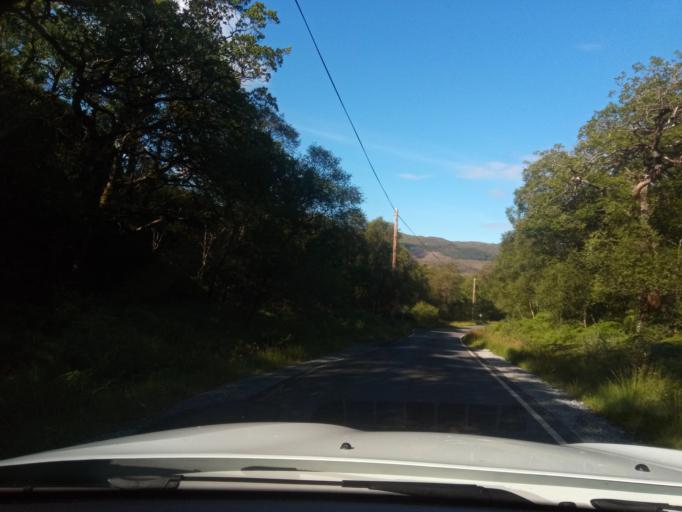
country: GB
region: Scotland
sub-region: Argyll and Bute
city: Isle Of Mull
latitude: 56.6928
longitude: -5.6735
